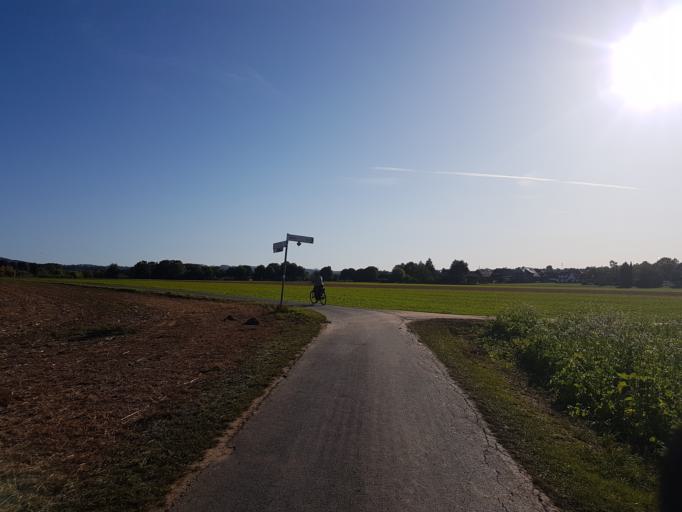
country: DE
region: North Rhine-Westphalia
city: Bad Oeynhausen
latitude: 52.2307
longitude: 8.8362
